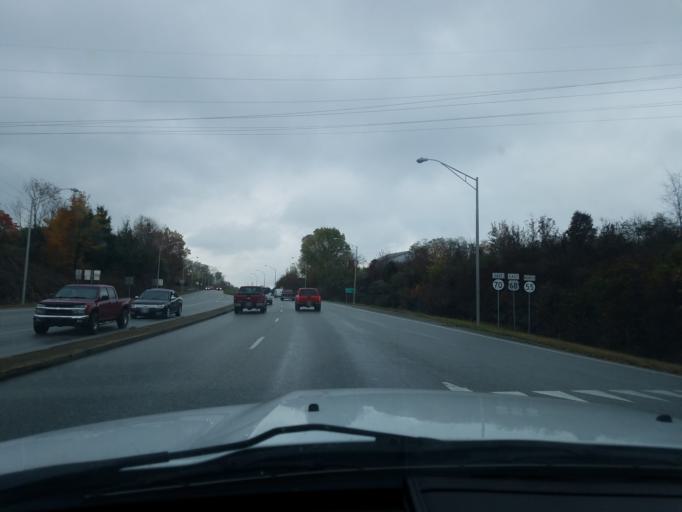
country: US
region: Kentucky
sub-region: Taylor County
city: Campbellsville
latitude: 37.3382
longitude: -85.3601
